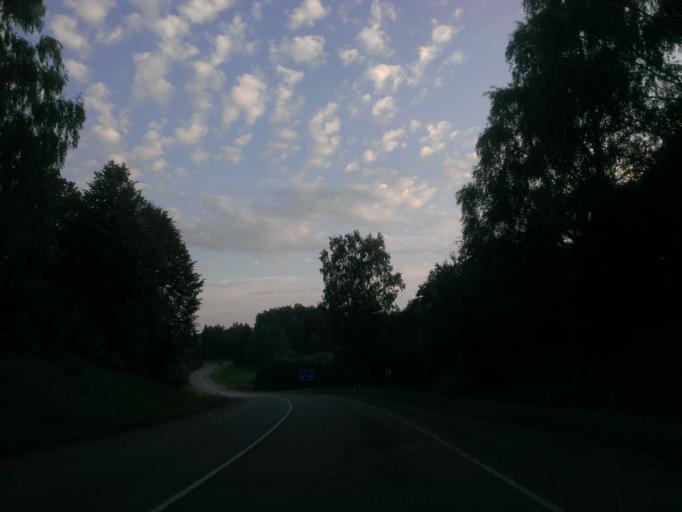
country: LV
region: Amatas Novads
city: Drabesi
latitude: 57.2358
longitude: 25.2747
